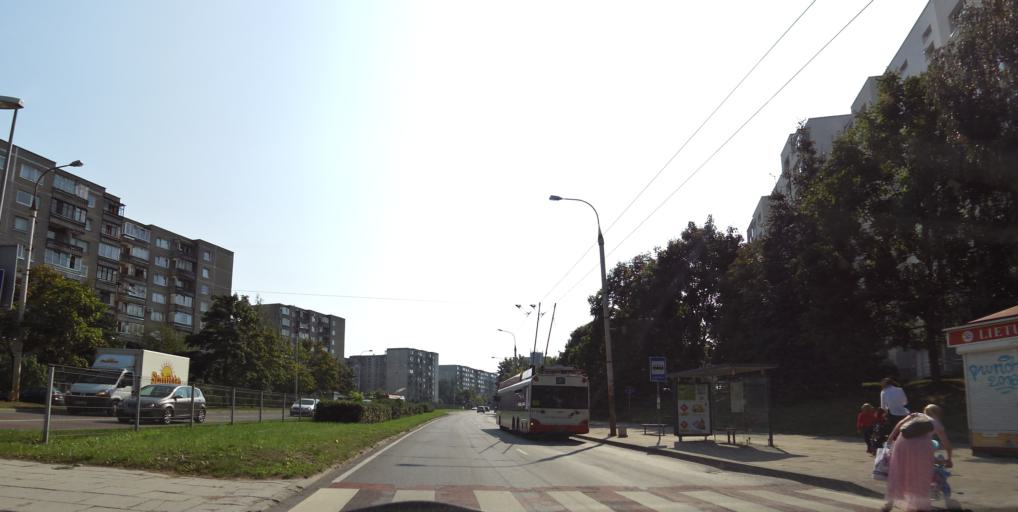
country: LT
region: Vilnius County
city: Justiniskes
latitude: 54.7226
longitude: 25.2218
